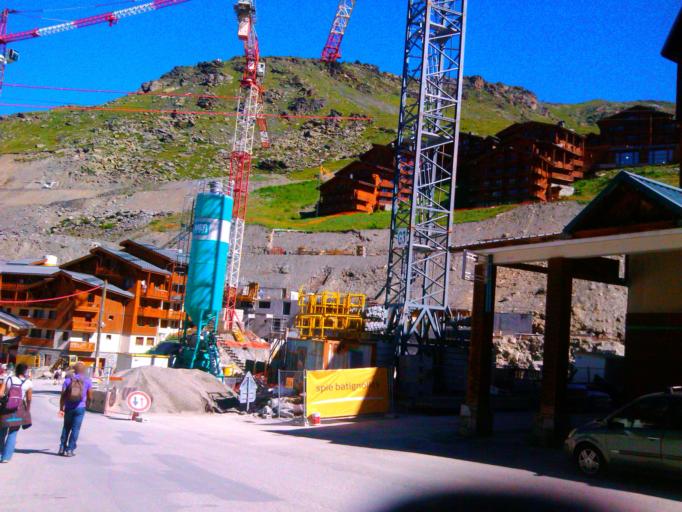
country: FR
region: Rhone-Alpes
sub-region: Departement de la Savoie
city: Val Thorens
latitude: 45.2986
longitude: 6.5780
